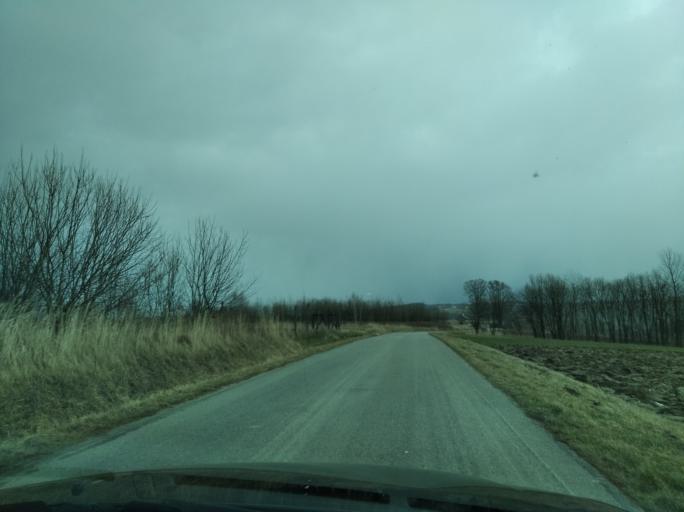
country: PL
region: Subcarpathian Voivodeship
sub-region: Powiat rzeszowski
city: Hyzne
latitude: 49.9033
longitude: 22.1774
